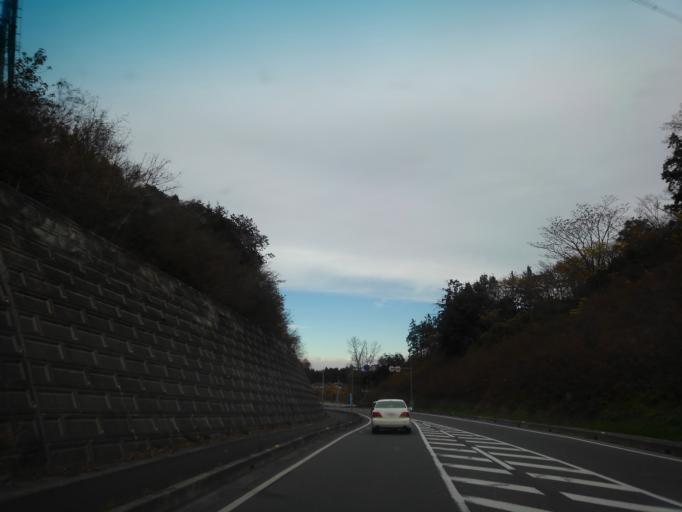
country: JP
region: Saitama
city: Morohongo
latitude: 35.9239
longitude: 139.3209
